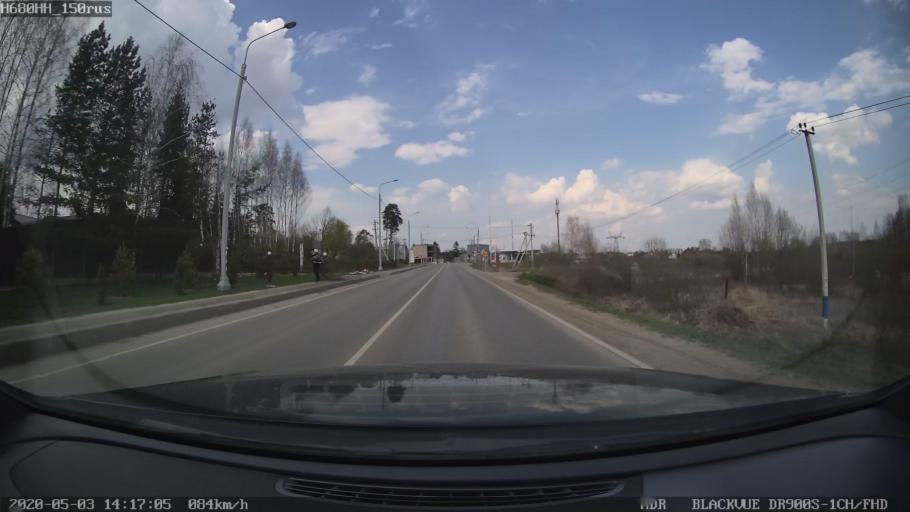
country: RU
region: Moskovskaya
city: Solnechnogorsk
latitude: 56.2055
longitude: 36.9631
